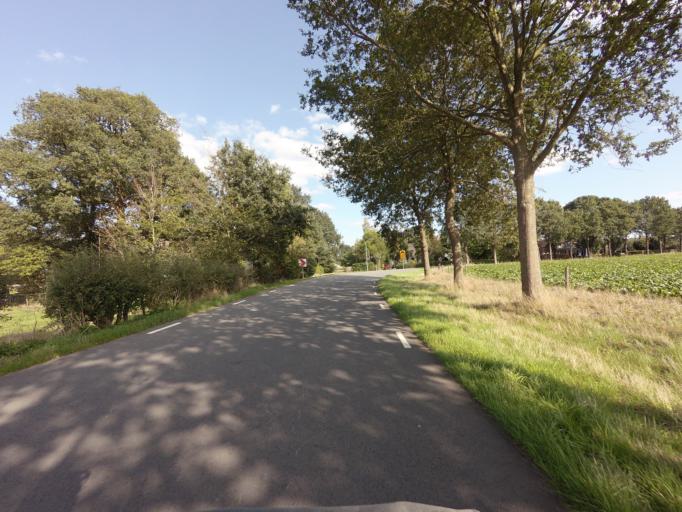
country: NL
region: Drenthe
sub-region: Gemeente Westerveld
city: Dwingeloo
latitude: 52.8330
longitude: 6.3911
